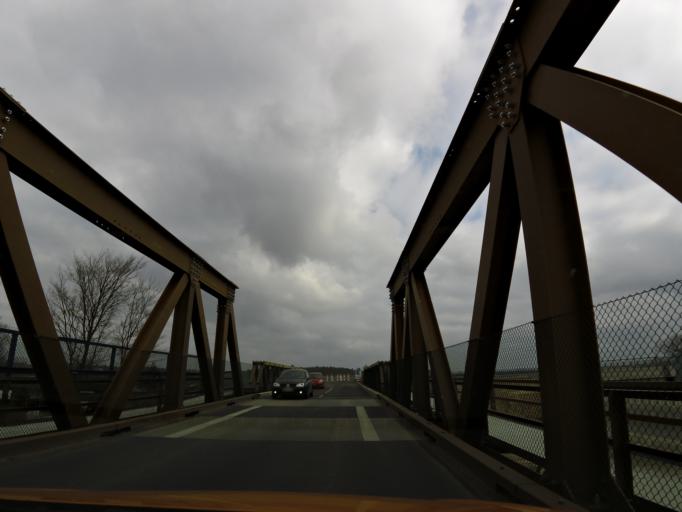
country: DE
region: Brandenburg
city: Werder
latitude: 52.4518
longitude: 12.9791
